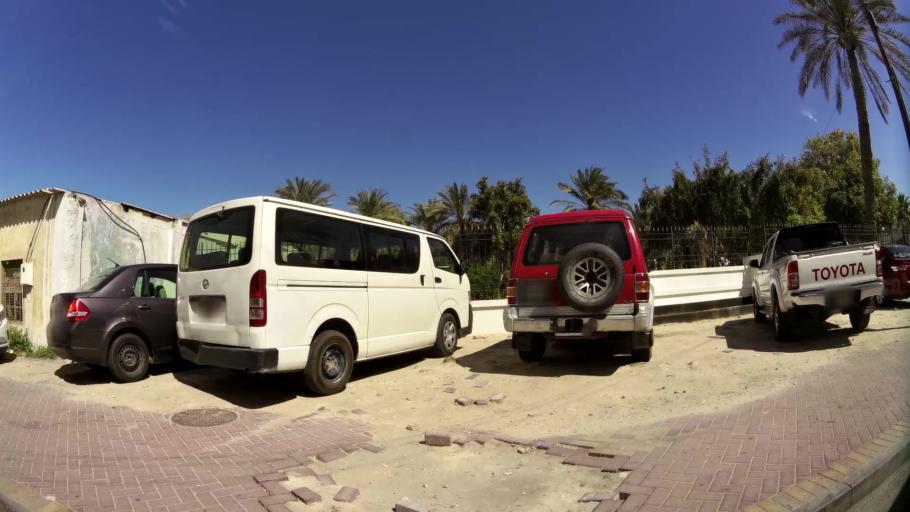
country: BH
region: Muharraq
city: Al Muharraq
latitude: 26.2590
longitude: 50.6147
